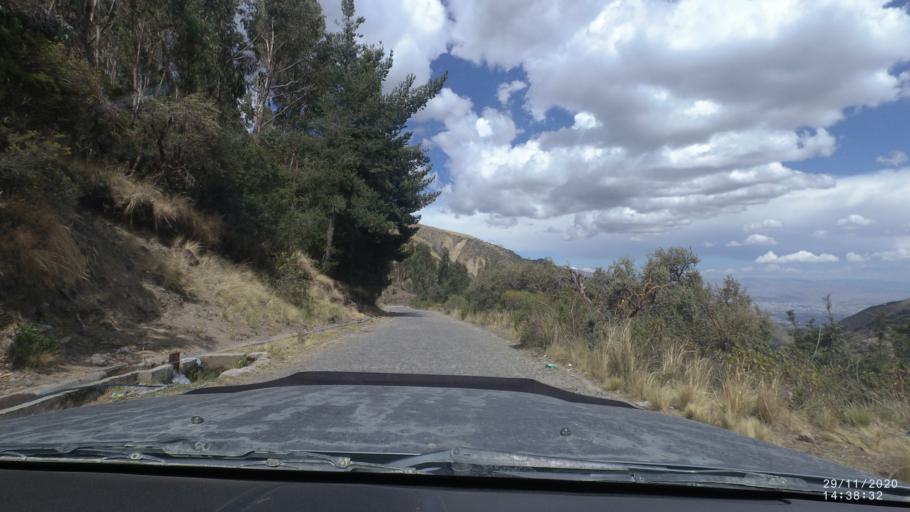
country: BO
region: Cochabamba
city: Sipe Sipe
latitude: -17.2725
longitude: -66.3295
